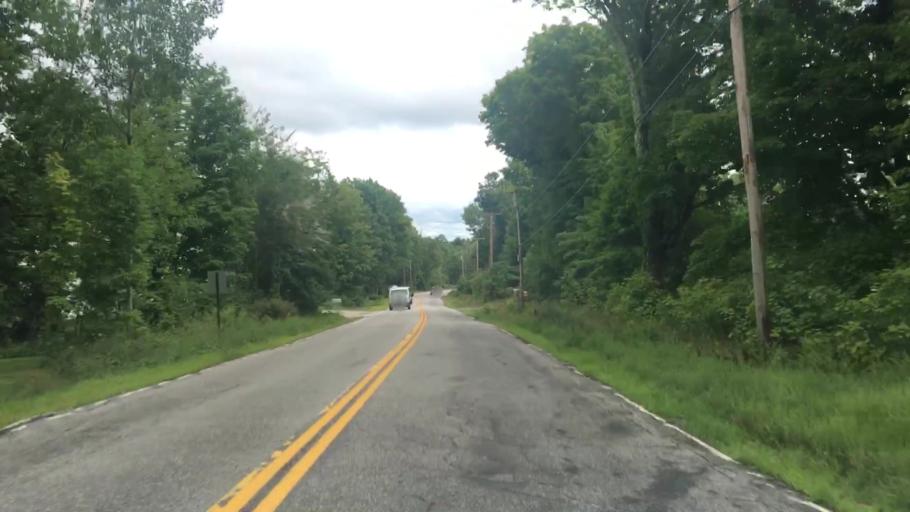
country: US
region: Maine
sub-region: York County
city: Limerick
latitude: 43.6778
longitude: -70.7856
